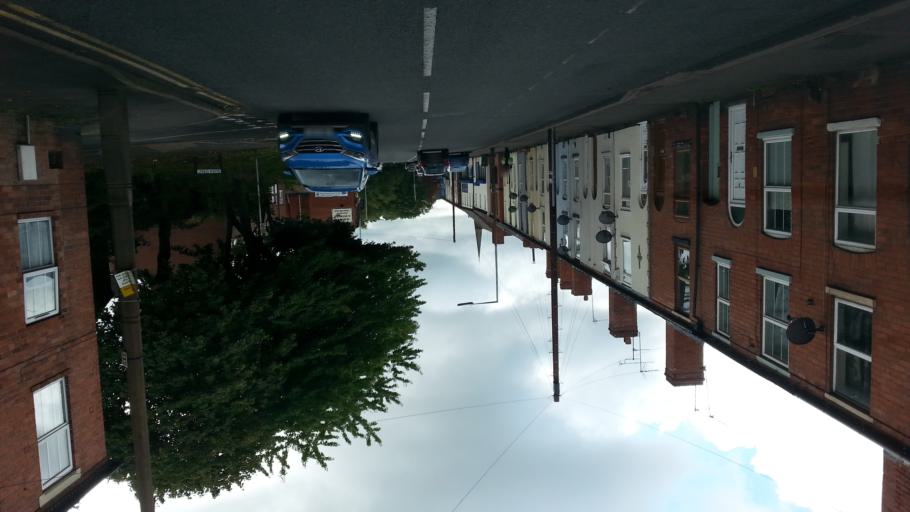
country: GB
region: England
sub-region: Dudley
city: Halesowen
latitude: 52.4520
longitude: -2.0552
